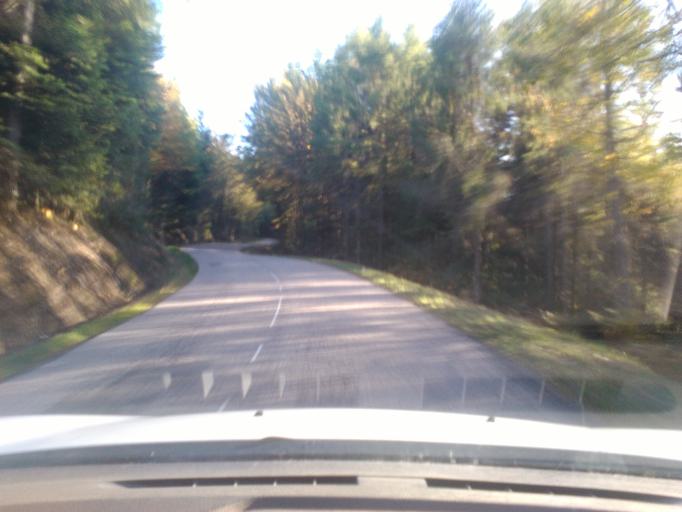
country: FR
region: Lorraine
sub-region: Departement des Vosges
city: Etival-Clairefontaine
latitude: 48.2928
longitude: 6.7844
